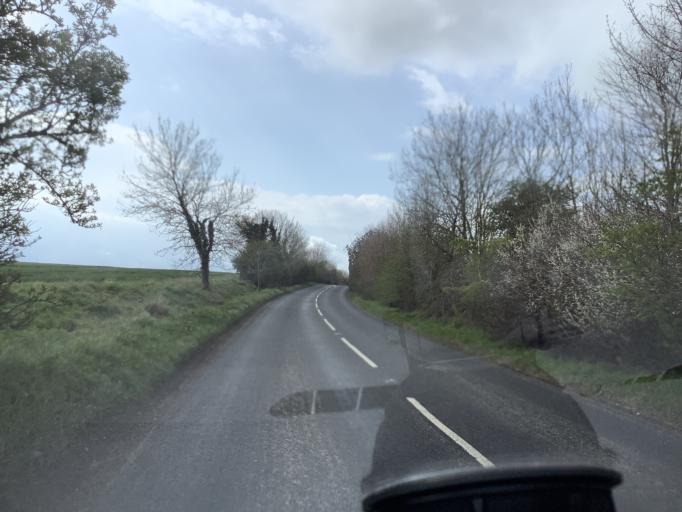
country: GB
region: England
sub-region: Borough of Swindon
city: Wroughton
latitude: 51.4906
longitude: -1.8394
